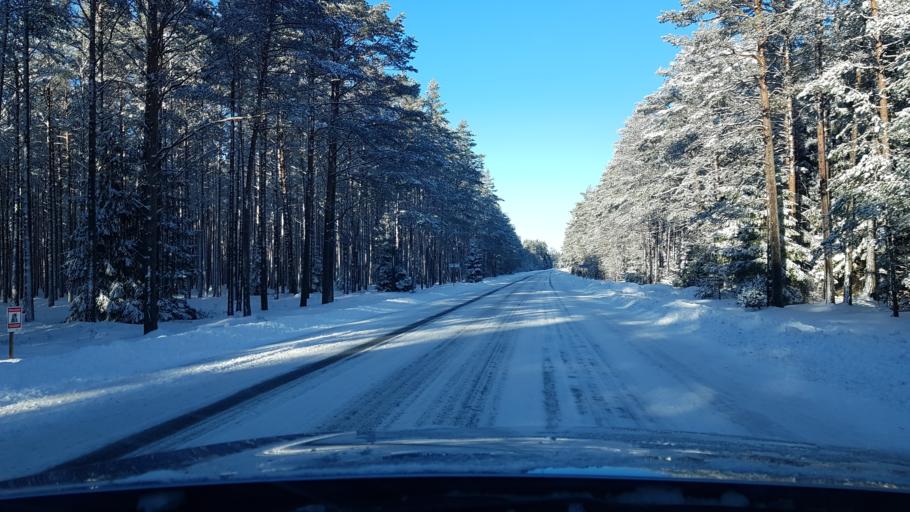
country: EE
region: Hiiumaa
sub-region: Kaerdla linn
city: Kardla
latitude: 58.9296
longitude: 22.7841
